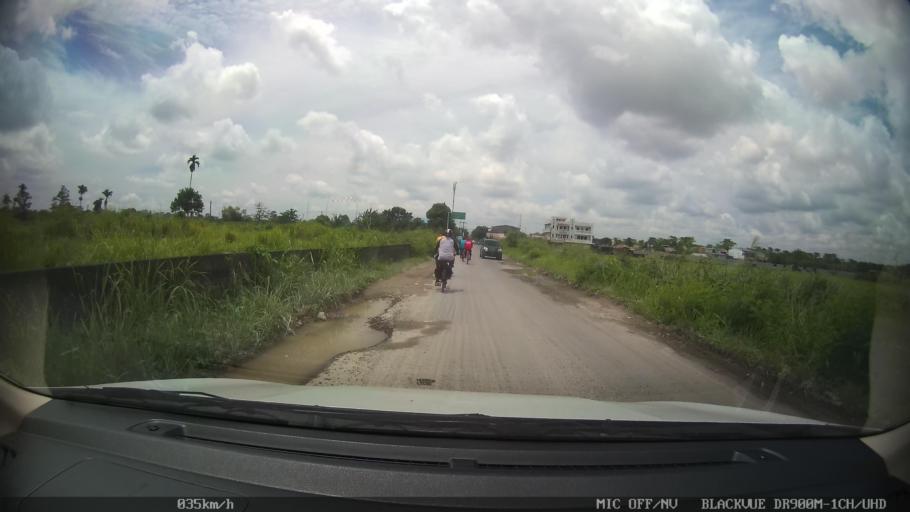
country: ID
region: North Sumatra
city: Medan
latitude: 3.6075
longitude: 98.7288
